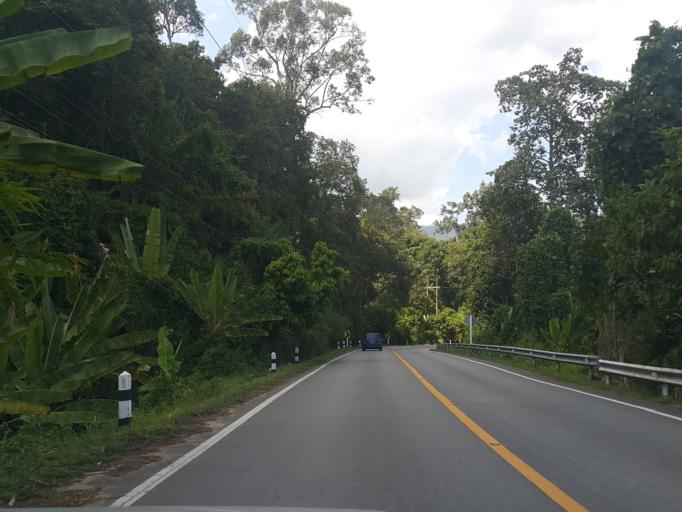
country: TH
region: Chiang Mai
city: Chom Thong
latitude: 18.5311
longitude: 98.6053
